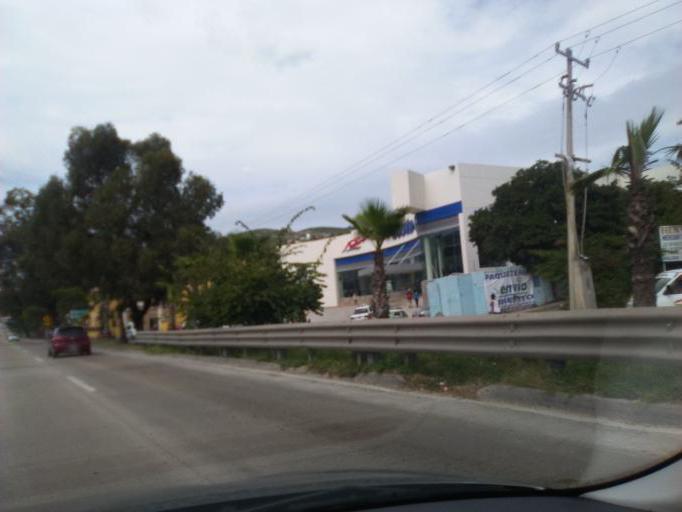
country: MX
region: Guerrero
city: Chilpancingo de los Bravos
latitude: 17.5614
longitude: -99.5104
